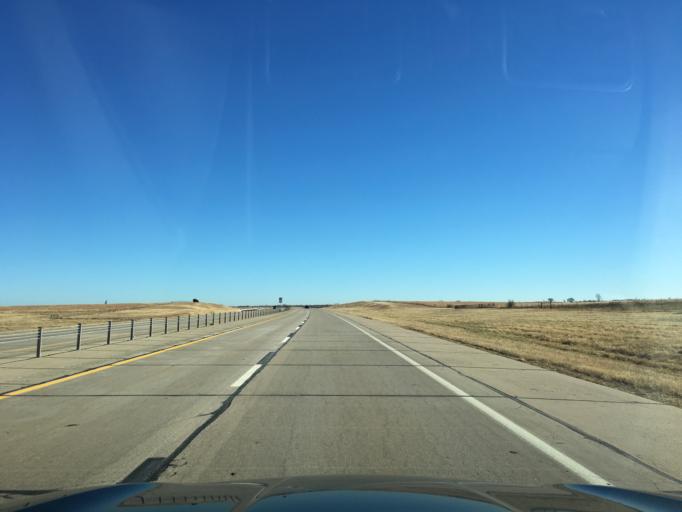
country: US
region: Oklahoma
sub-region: Noble County
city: Perry
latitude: 36.3951
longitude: -97.2217
